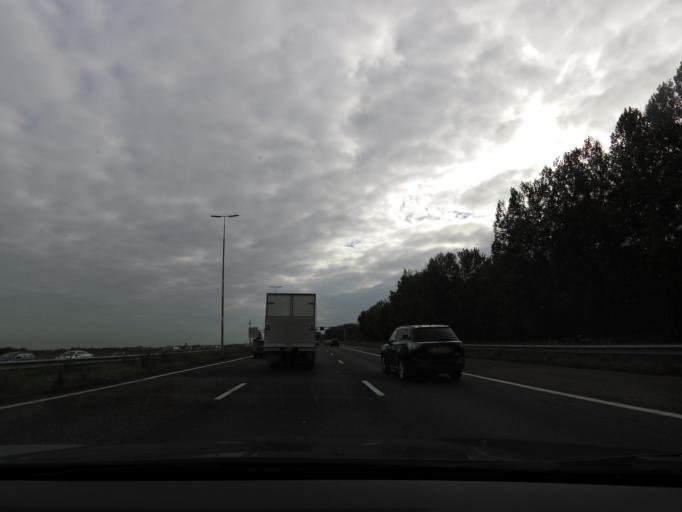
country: NL
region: South Holland
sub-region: Gemeente Voorschoten
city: Voorschoten
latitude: 52.1207
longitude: 4.4746
